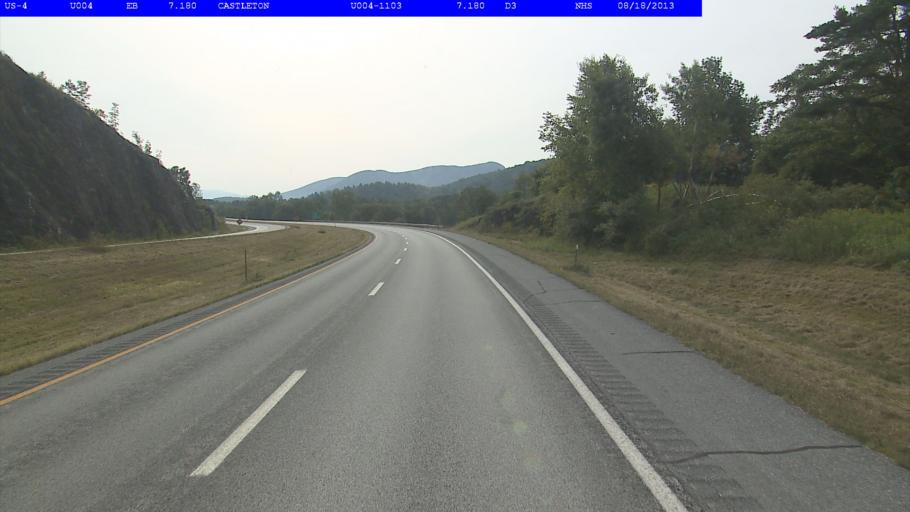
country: US
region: Vermont
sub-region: Rutland County
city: Castleton
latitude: 43.6170
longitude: -73.1771
